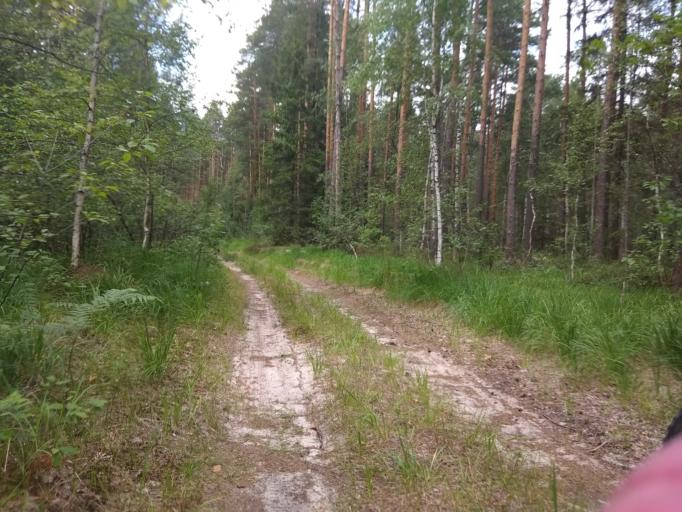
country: RU
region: Moskovskaya
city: Misheronskiy
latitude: 55.6392
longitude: 39.7115
